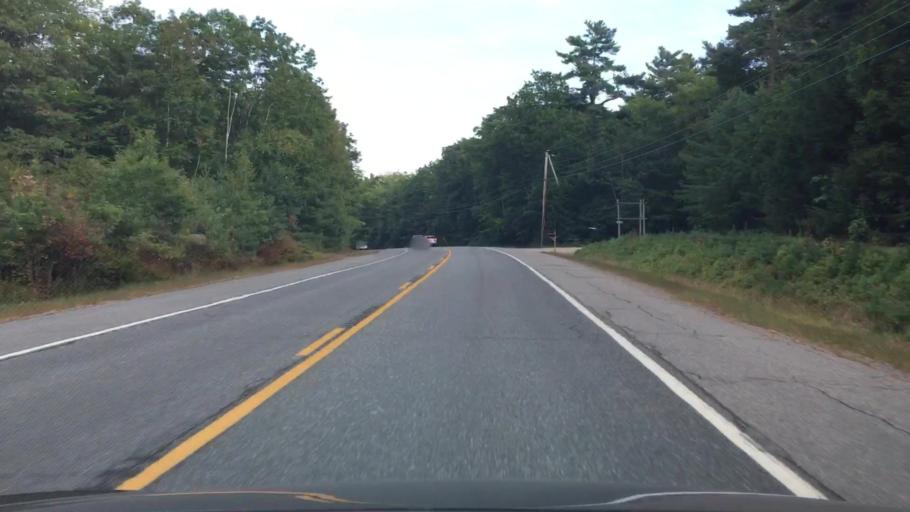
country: US
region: Maine
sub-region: Hancock County
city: Orland
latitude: 44.5646
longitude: -68.6665
